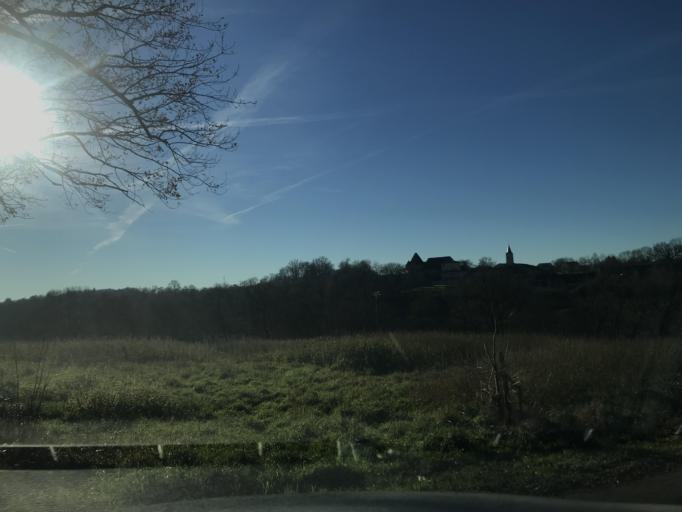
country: FR
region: Poitou-Charentes
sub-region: Departement de la Charente
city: Saint-Claud
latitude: 45.8518
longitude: 0.5135
